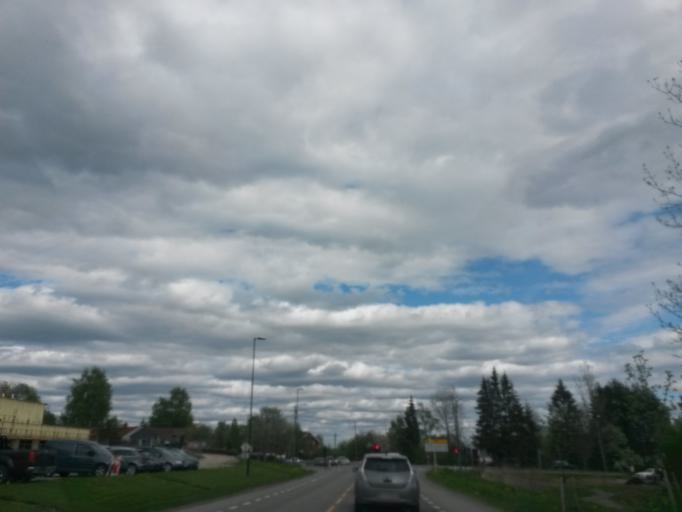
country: NO
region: Akershus
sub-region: Asker
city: Asker
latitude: 59.8293
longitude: 10.4400
